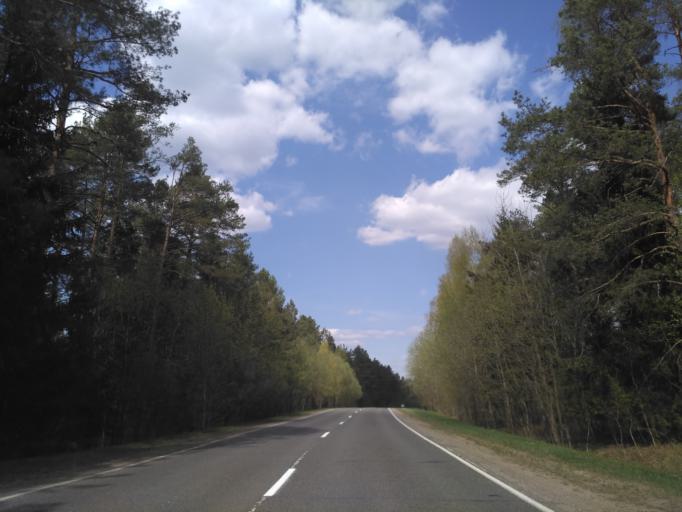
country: BY
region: Minsk
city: Myadzyel
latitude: 54.7657
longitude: 26.9470
